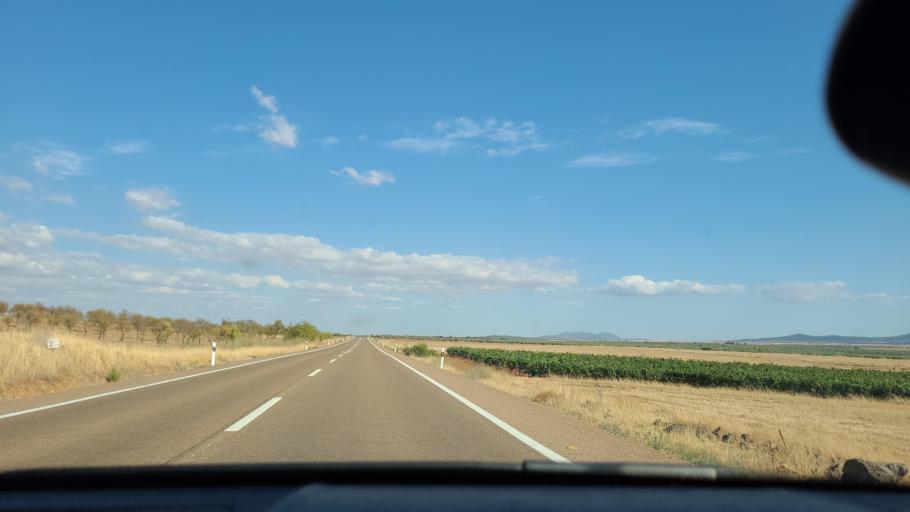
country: ES
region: Extremadura
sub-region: Provincia de Badajoz
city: Usagre
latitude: 38.3559
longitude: -6.2066
